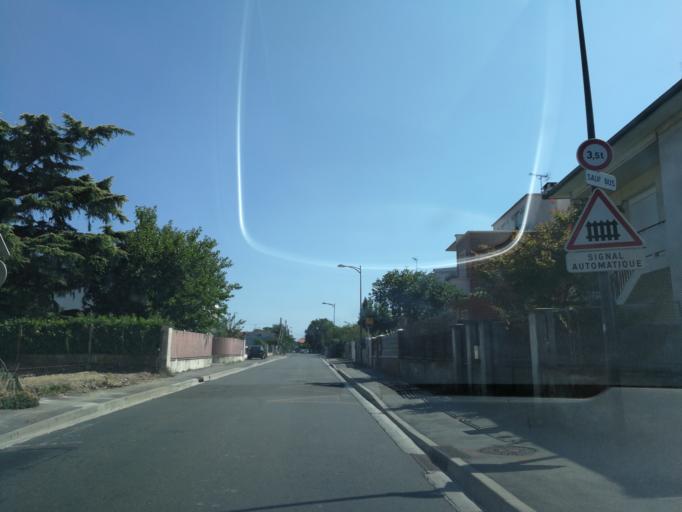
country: FR
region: Midi-Pyrenees
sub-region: Departement de la Haute-Garonne
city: L'Union
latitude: 43.6329
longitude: 1.4700
